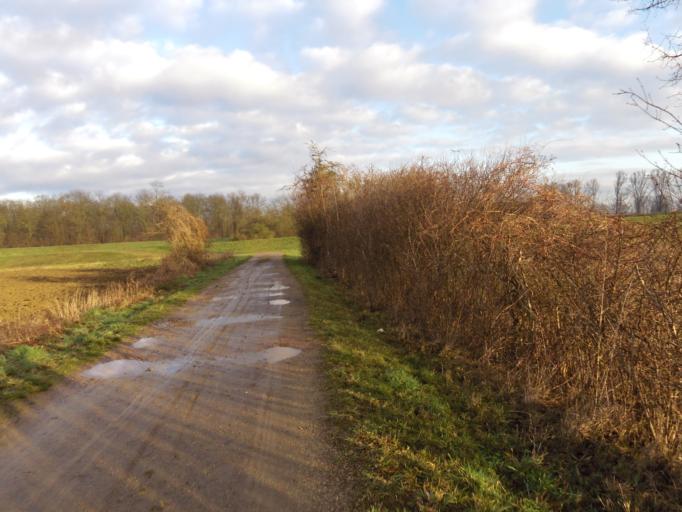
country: DE
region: Rheinland-Pfalz
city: Bobenheim-Roxheim
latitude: 49.6042
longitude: 8.4006
